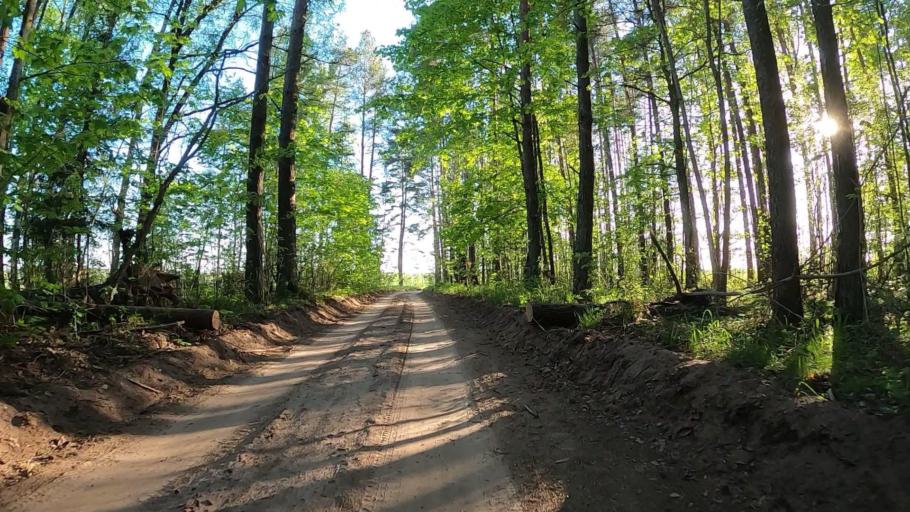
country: LV
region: Kekava
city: Kekava
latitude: 56.7585
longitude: 24.2629
